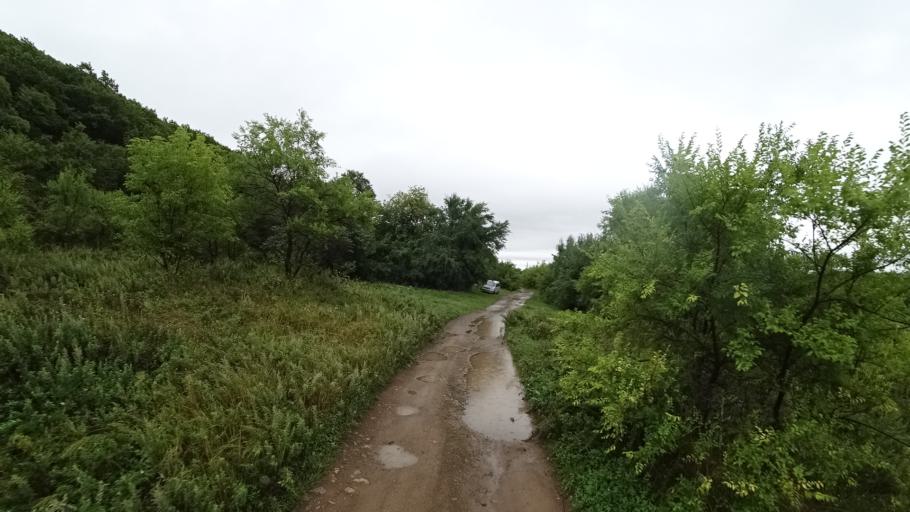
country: RU
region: Primorskiy
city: Monastyrishche
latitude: 44.2662
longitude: 132.4041
